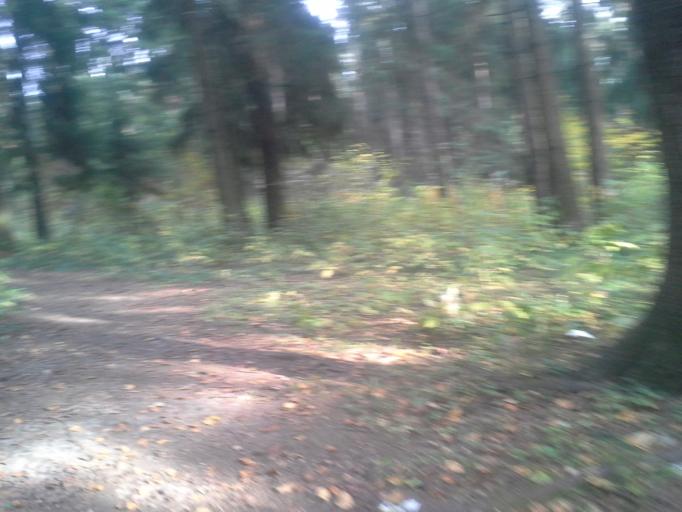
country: RU
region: Moskovskaya
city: Selyatino
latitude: 55.4673
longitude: 36.9435
